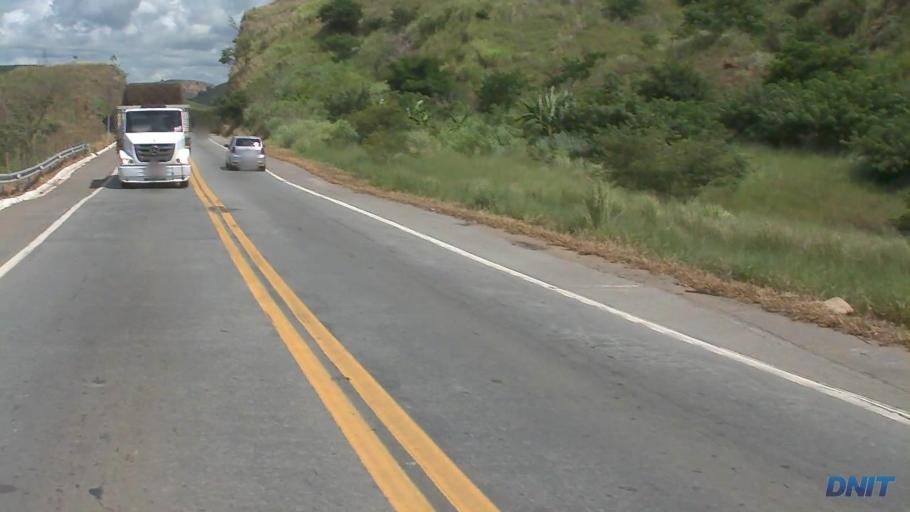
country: BR
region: Minas Gerais
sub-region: Governador Valadares
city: Governador Valadares
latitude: -18.9289
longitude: -42.0431
